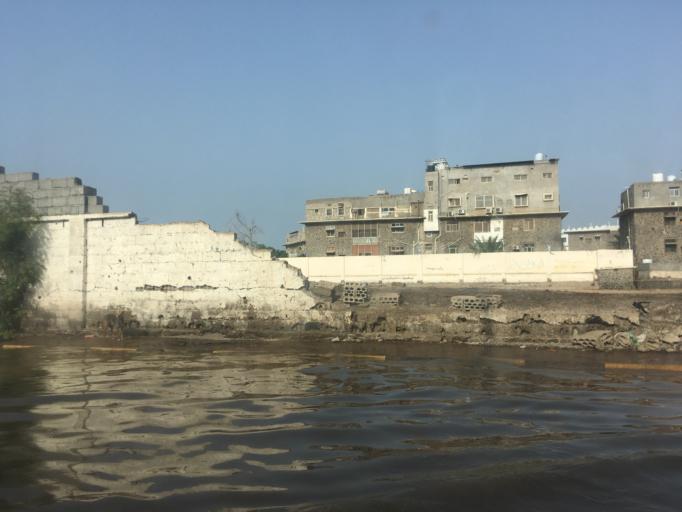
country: YE
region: Aden
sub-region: Attawahi
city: At Tawahi
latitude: 12.7790
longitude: 44.9799
